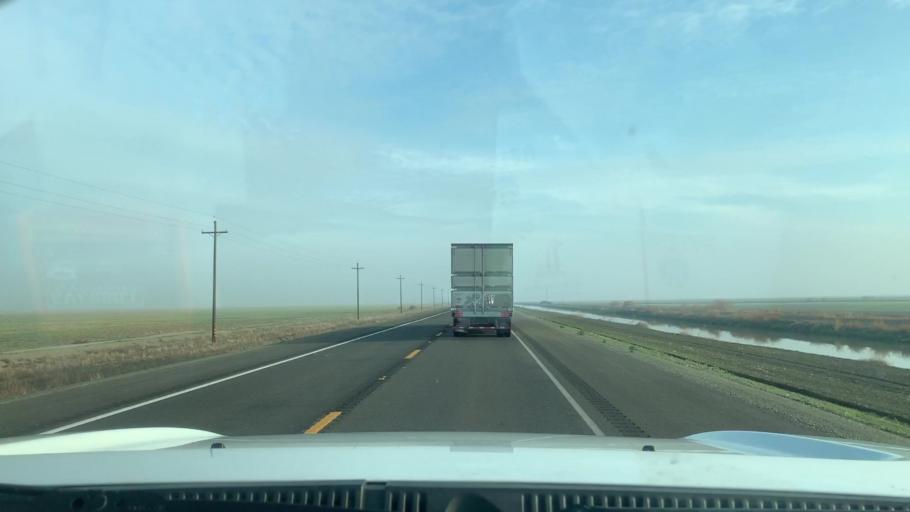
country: US
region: California
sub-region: Kings County
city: Kettleman City
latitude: 36.0622
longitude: -119.9375
